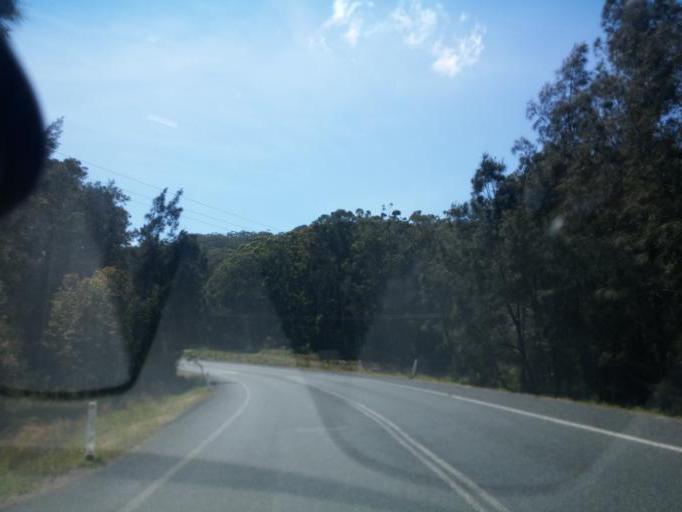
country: AU
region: New South Wales
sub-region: Great Lakes
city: Forster
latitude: -32.3392
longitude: 152.5221
